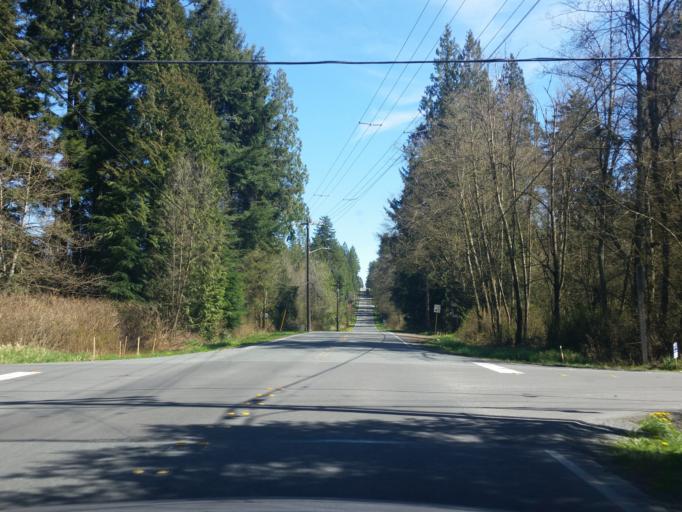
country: US
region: Washington
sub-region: Snohomish County
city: North Creek
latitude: 47.8344
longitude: -122.1645
